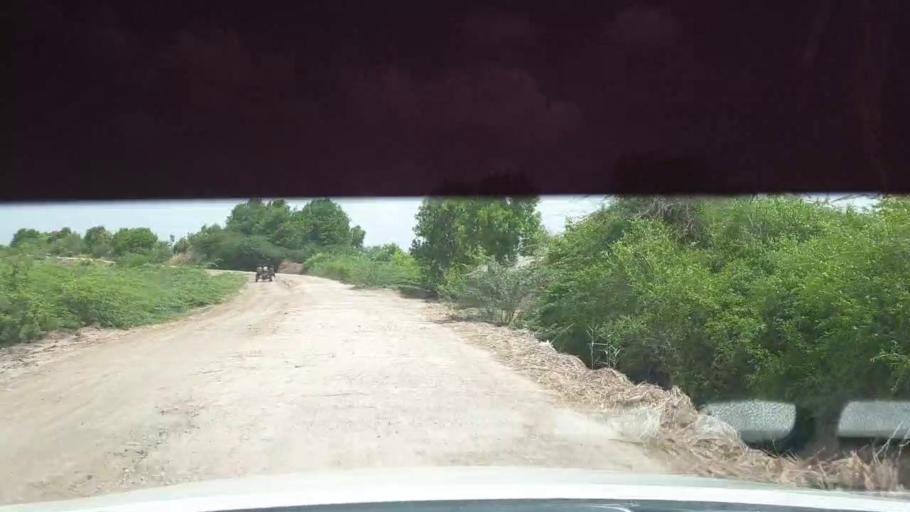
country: PK
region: Sindh
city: Kadhan
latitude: 24.4937
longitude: 68.9826
